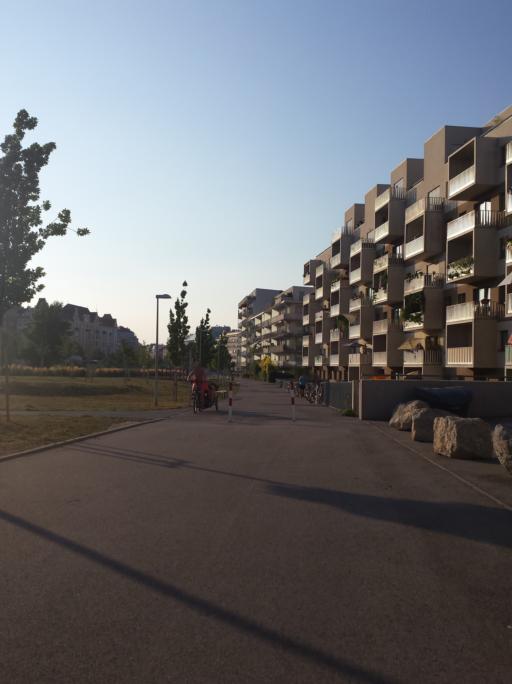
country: AT
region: Vienna
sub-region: Wien Stadt
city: Vienna
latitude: 48.1903
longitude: 16.3941
